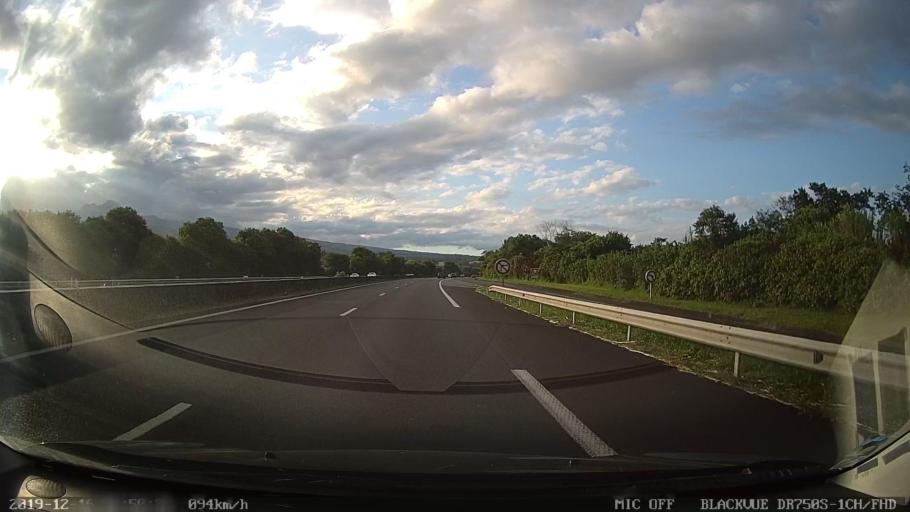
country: RE
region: Reunion
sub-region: Reunion
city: Bras-Panon
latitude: -21.0142
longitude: 55.6922
